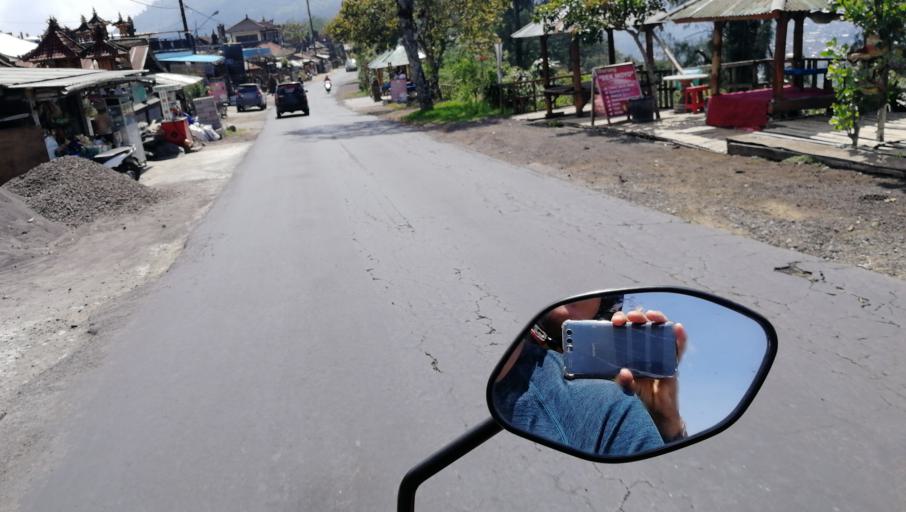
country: ID
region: Bali
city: Munduk
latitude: -8.2365
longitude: 115.1345
